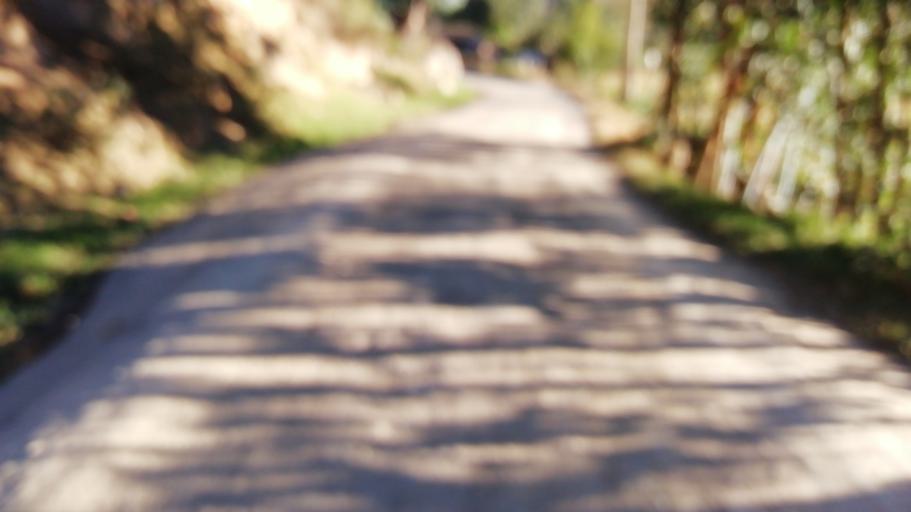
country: CO
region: Boyaca
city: Gameza
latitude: 5.7867
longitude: -72.8010
